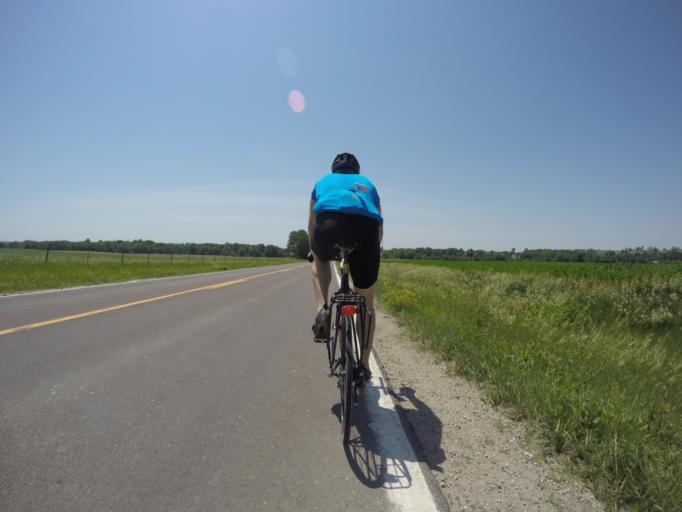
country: US
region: Nebraska
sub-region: Pawnee County
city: Pawnee City
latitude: 40.0308
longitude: -96.0482
